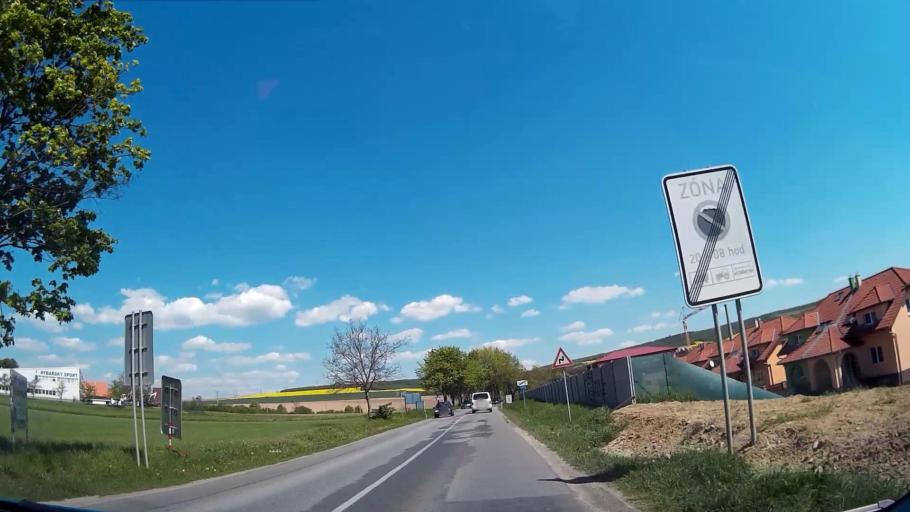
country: CZ
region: South Moravian
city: Ivancice
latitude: 49.1078
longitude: 16.3728
